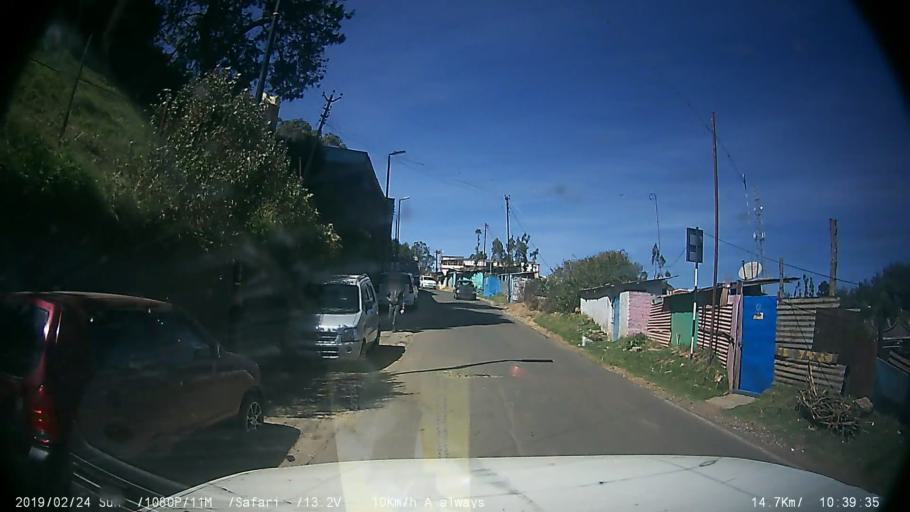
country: IN
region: Tamil Nadu
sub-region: Nilgiri
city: Ooty
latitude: 11.4101
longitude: 76.6947
